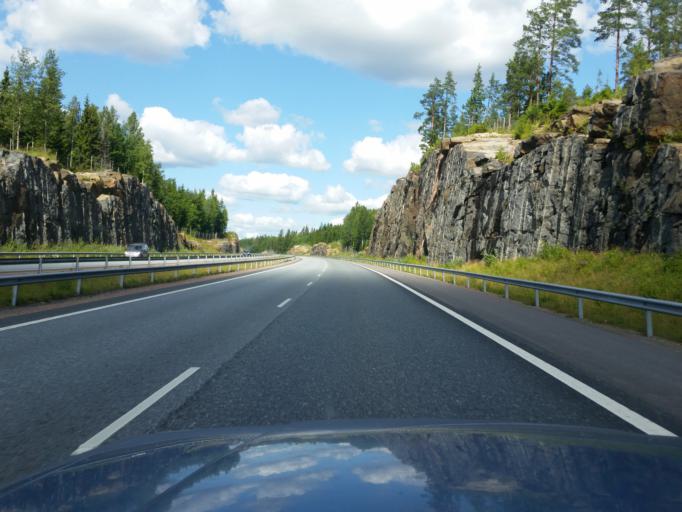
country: FI
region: Uusimaa
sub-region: Helsinki
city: Sammatti
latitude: 60.3586
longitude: 23.8889
